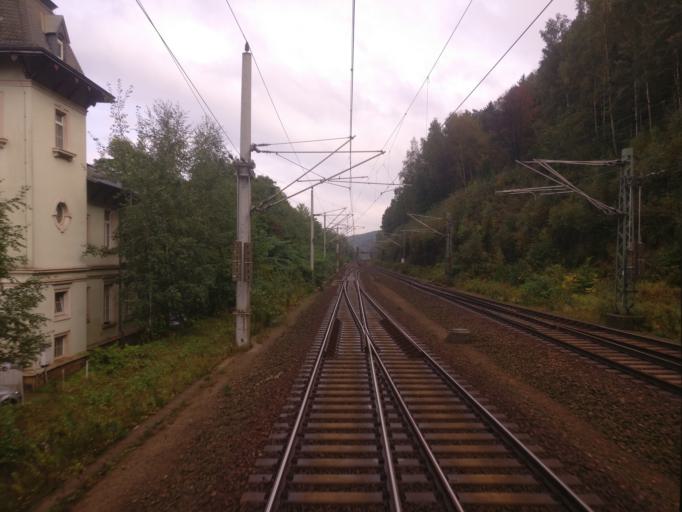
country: DE
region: Saxony
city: Bad Schandau
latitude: 50.9177
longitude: 14.1436
